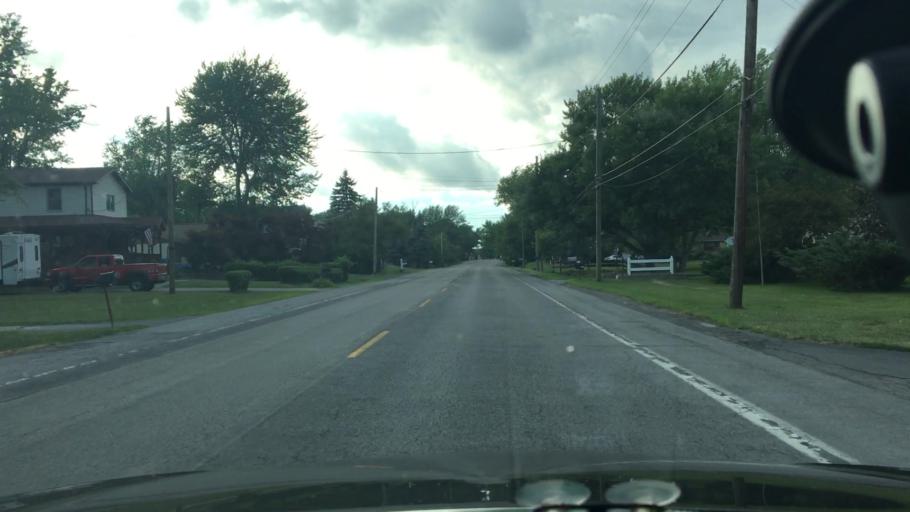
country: US
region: New York
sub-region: Erie County
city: Depew
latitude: 42.8364
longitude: -78.7147
